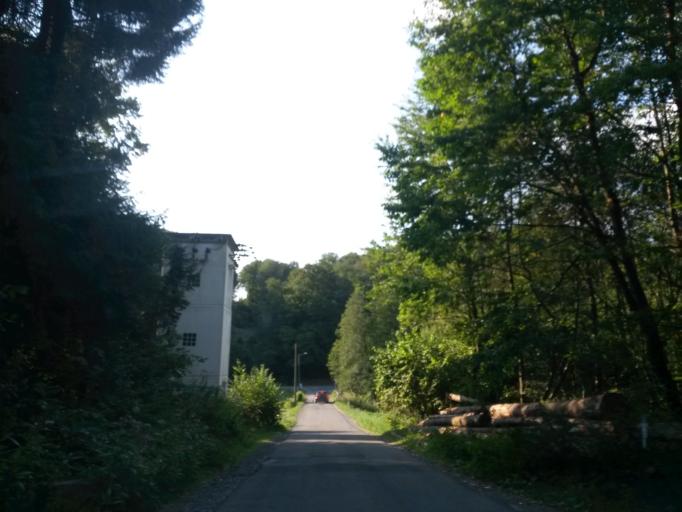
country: DE
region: North Rhine-Westphalia
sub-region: Regierungsbezirk Koln
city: Lindlar
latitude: 50.9943
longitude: 7.3330
